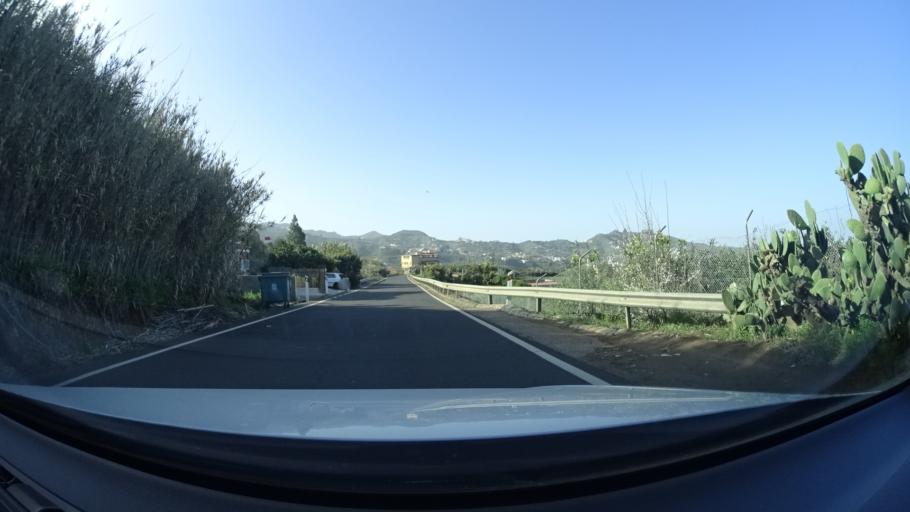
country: ES
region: Canary Islands
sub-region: Provincia de Las Palmas
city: Vega de San Mateo
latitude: 28.0140
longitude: -15.5359
